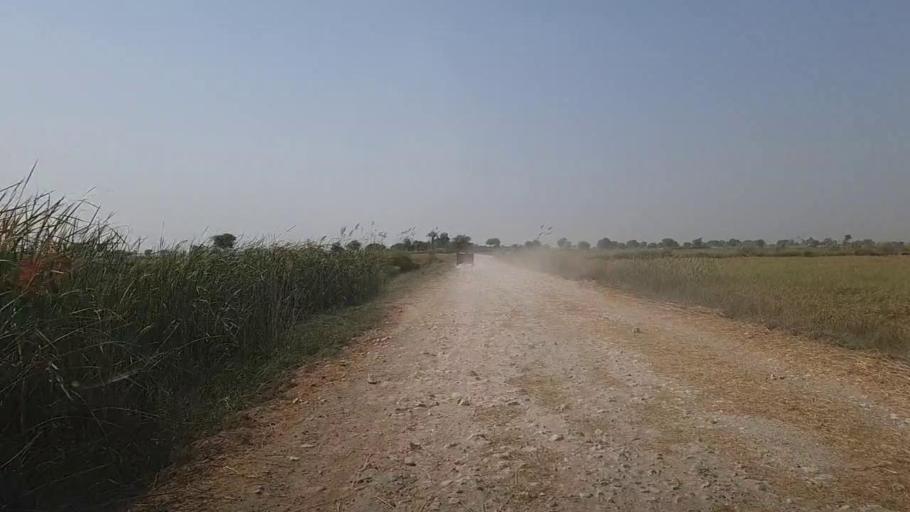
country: PK
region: Sindh
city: Kandhkot
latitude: 28.3924
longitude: 69.3069
